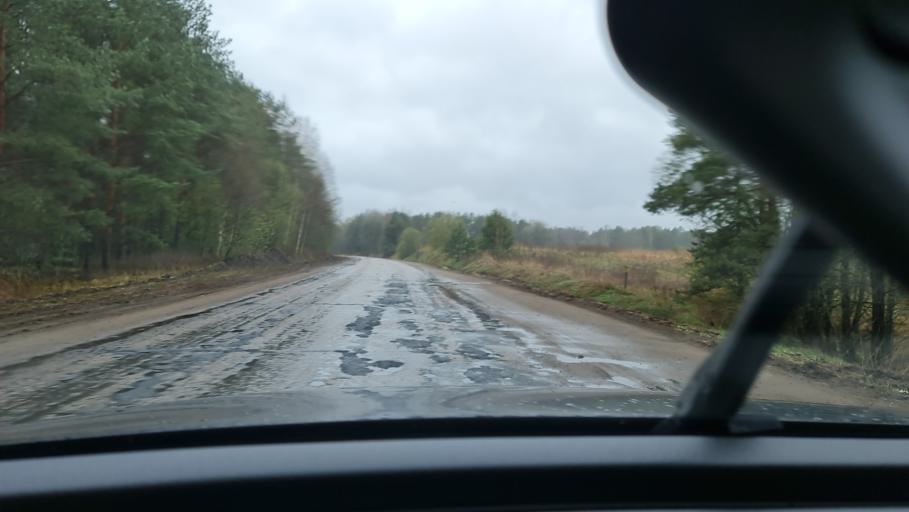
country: RU
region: Novgorod
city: Valday
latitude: 58.0407
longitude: 32.9214
